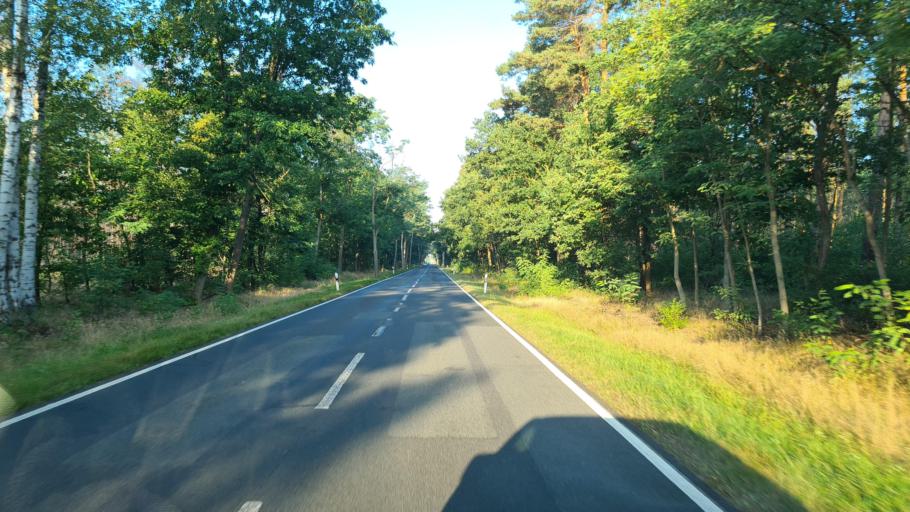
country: DE
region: Brandenburg
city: Juterbog
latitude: 52.0942
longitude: 13.0451
